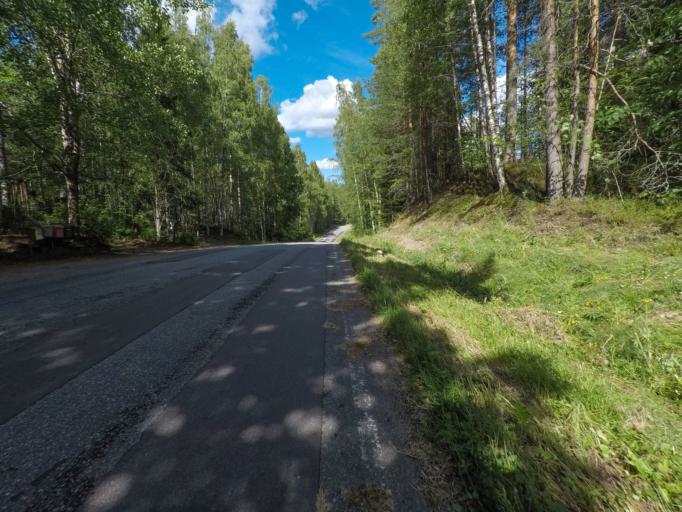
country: FI
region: South Karelia
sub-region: Lappeenranta
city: Joutseno
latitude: 61.1239
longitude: 28.3884
